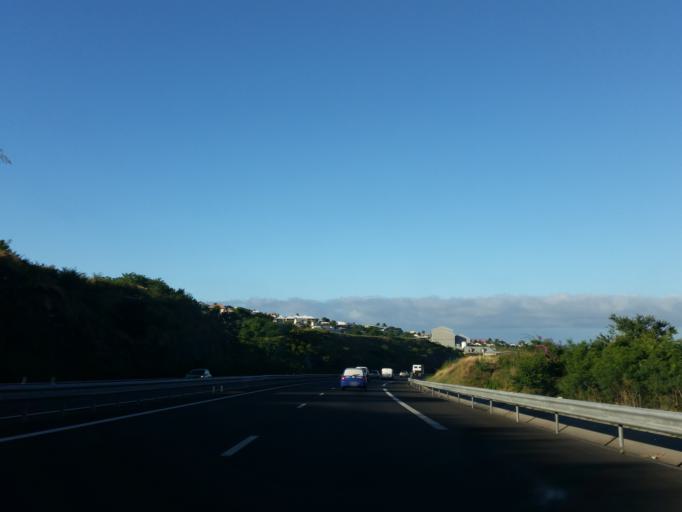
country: RE
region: Reunion
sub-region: Reunion
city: Saint-Leu
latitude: -21.1940
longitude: 55.2962
